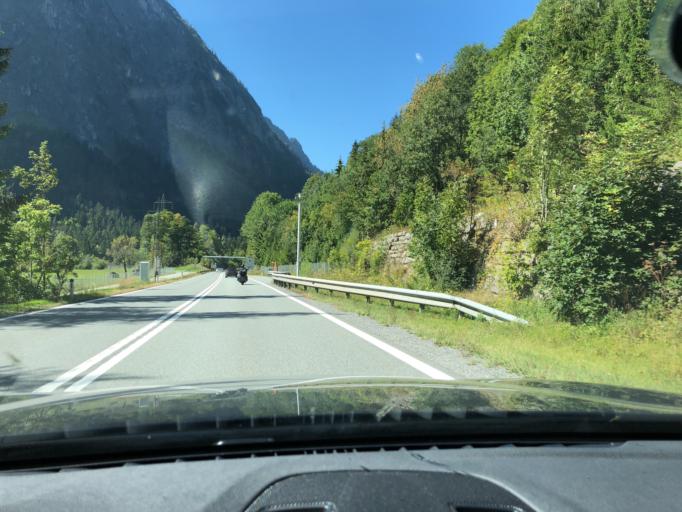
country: AT
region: Vorarlberg
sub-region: Politischer Bezirk Bludenz
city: Dalaas
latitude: 47.1298
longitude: 9.9687
